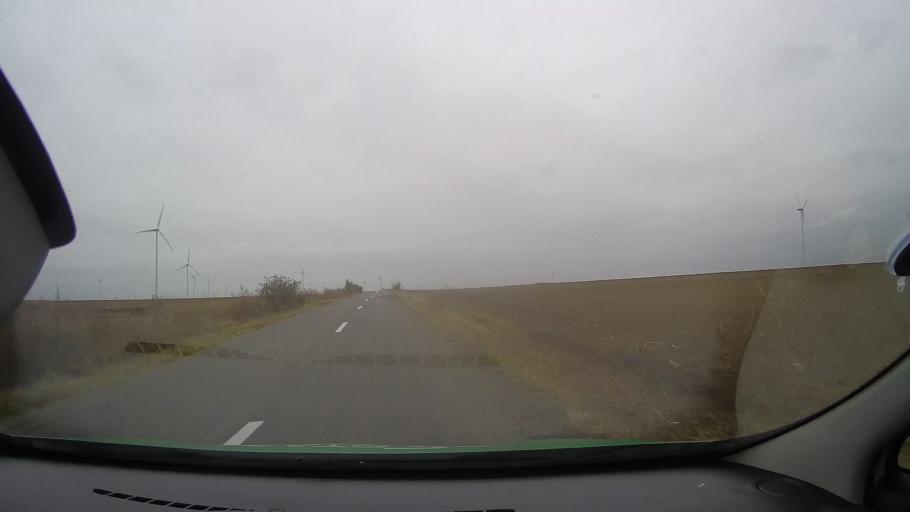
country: RO
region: Constanta
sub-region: Comuna Pantelimon
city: Pantelimon
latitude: 44.5080
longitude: 28.3429
